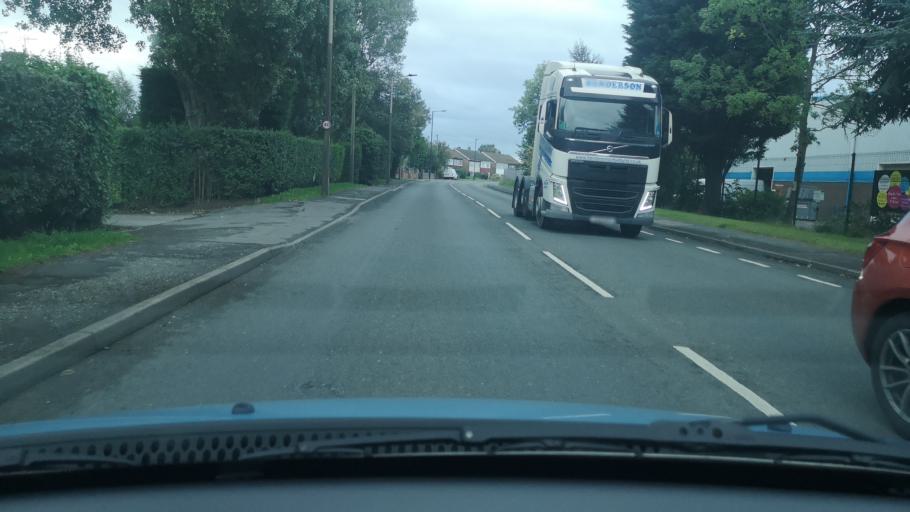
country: GB
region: England
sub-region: Doncaster
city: Kirk Sandall
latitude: 53.5614
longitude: -1.0728
